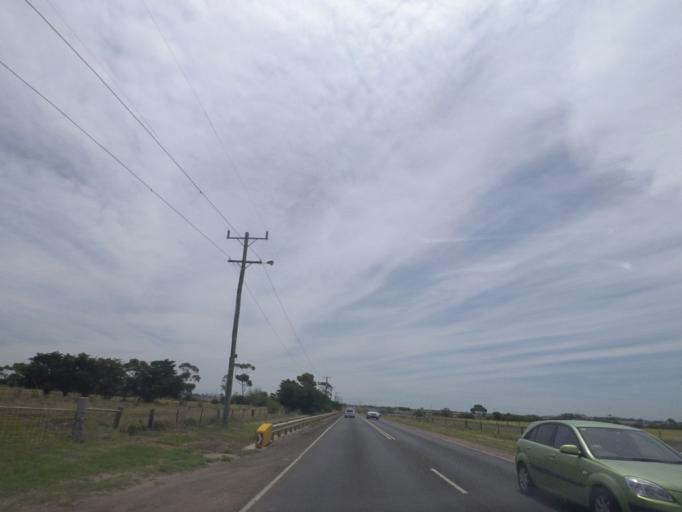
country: AU
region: Victoria
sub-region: Wyndham
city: Tarneit
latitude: -37.8253
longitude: 144.6926
